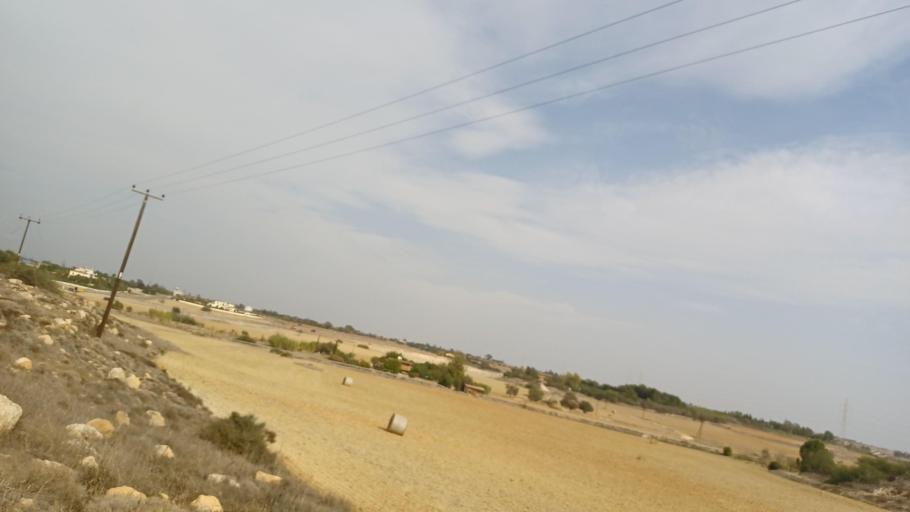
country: CY
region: Ammochostos
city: Frenaros
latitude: 35.0536
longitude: 33.8824
